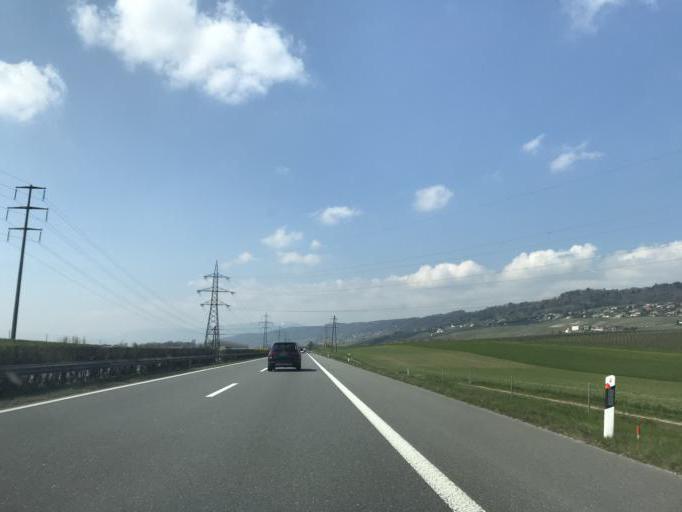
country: CH
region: Vaud
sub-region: Morges District
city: Aubonne
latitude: 46.4770
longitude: 6.3917
